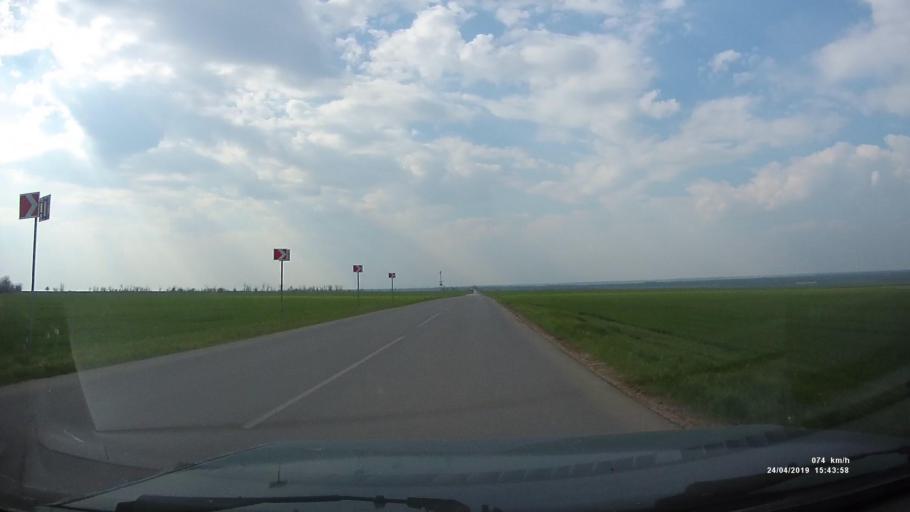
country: RU
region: Kalmykiya
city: Yashalta
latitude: 46.5860
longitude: 42.7634
